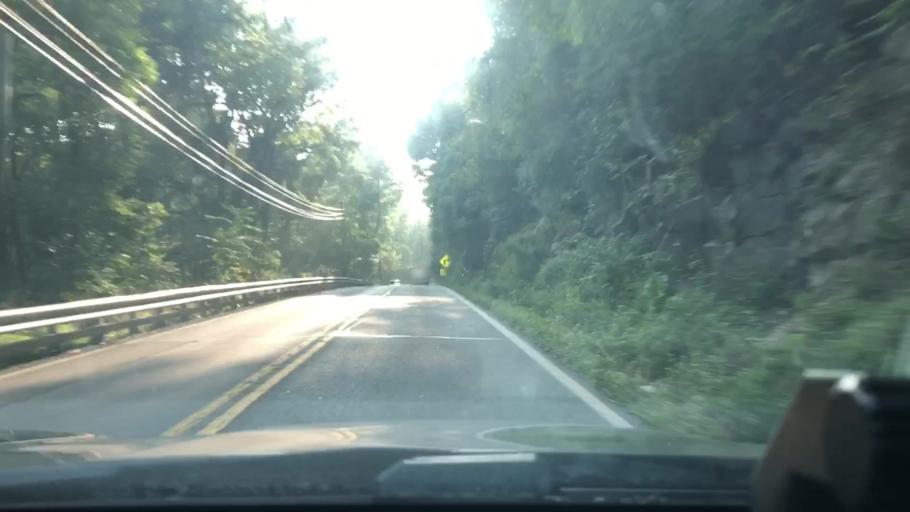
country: US
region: Pennsylvania
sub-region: Berks County
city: Kutztown
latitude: 40.5378
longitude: -75.7960
